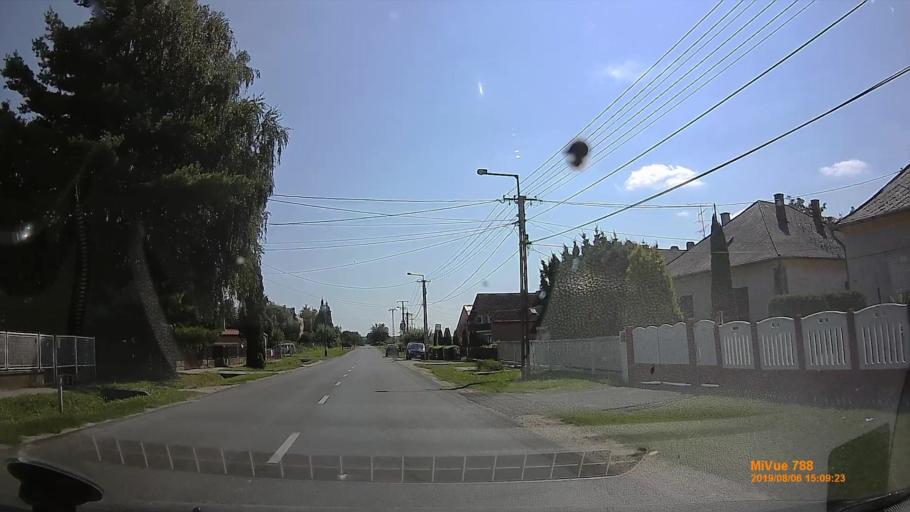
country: HU
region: Zala
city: Nagykanizsa
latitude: 46.4048
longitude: 16.9832
